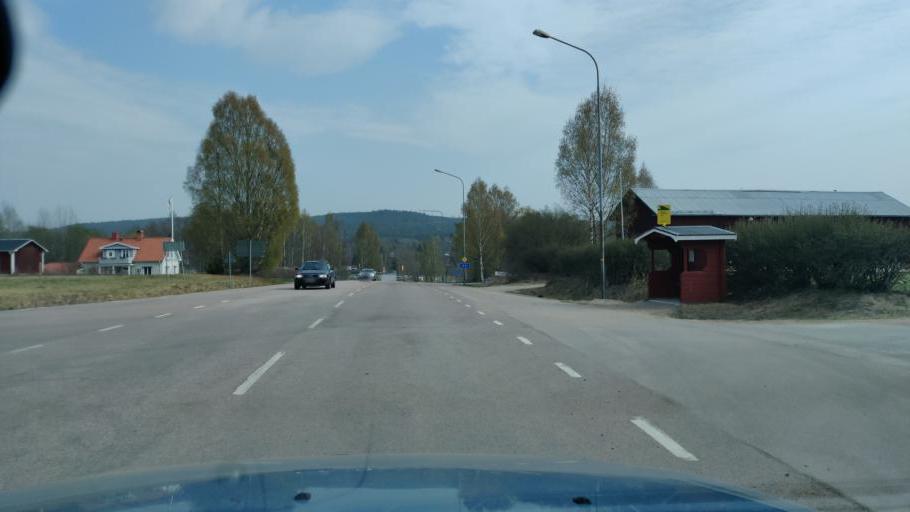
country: SE
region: Vaermland
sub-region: Munkfors Kommun
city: Munkfors
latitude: 59.8303
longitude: 13.5211
